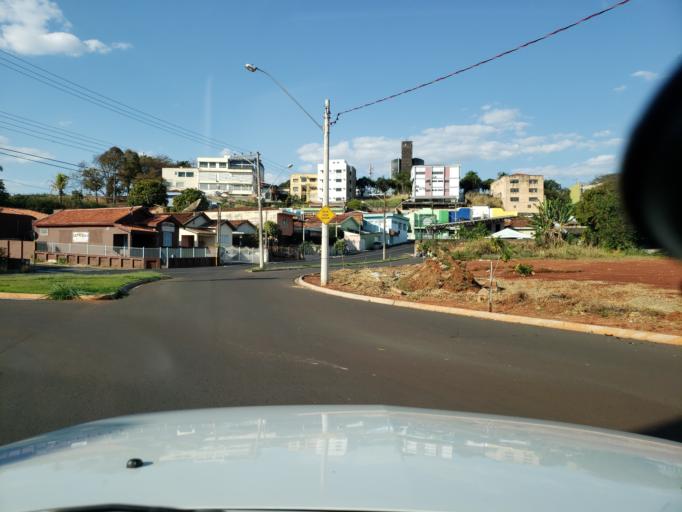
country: BR
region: Sao Paulo
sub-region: Moji-Guacu
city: Mogi-Gaucu
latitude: -22.3694
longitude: -46.9468
